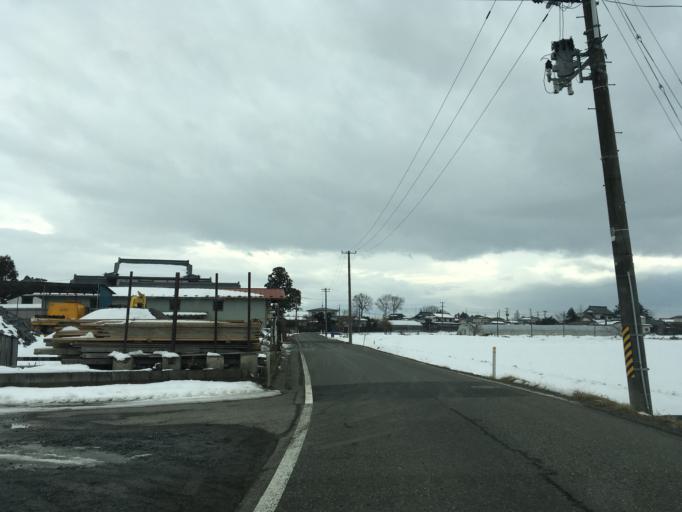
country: JP
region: Iwate
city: Ichinoseki
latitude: 38.7811
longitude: 141.1517
